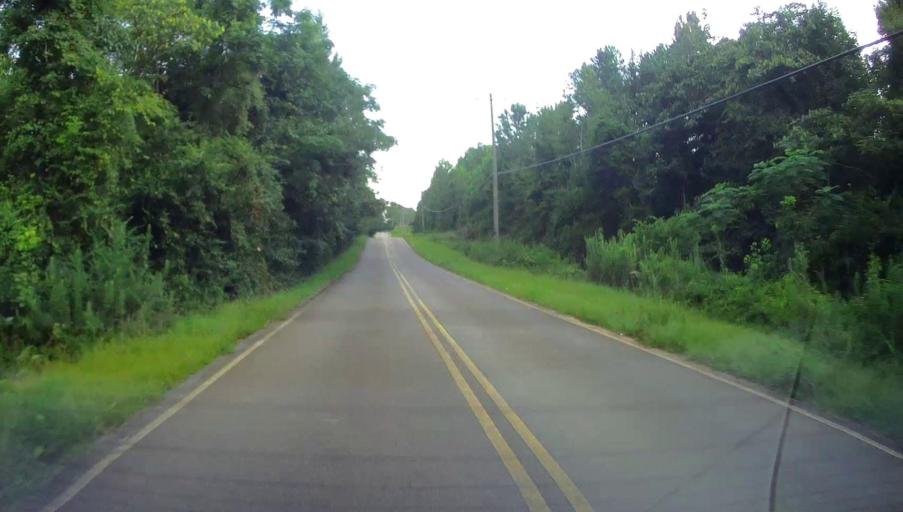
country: US
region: Georgia
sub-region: Houston County
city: Centerville
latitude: 32.5900
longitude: -83.6524
